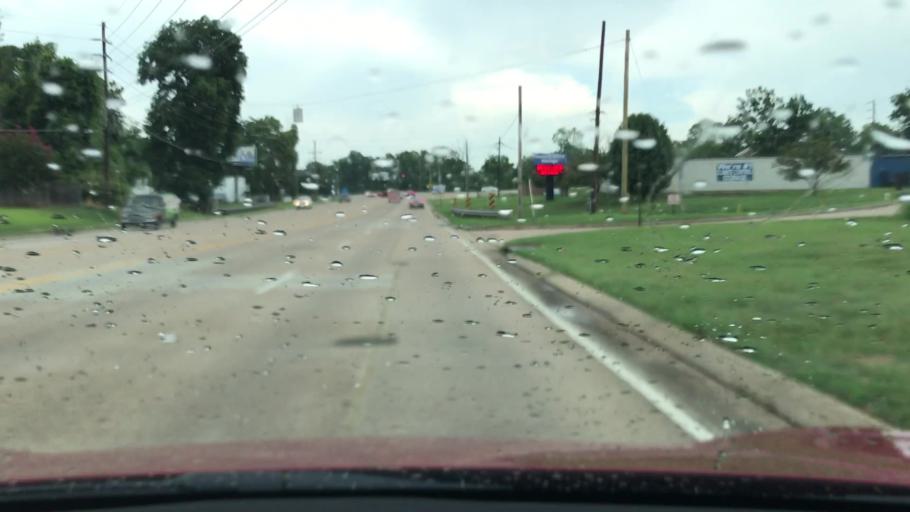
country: US
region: Louisiana
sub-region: Bossier Parish
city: Bossier City
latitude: 32.4453
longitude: -93.7048
